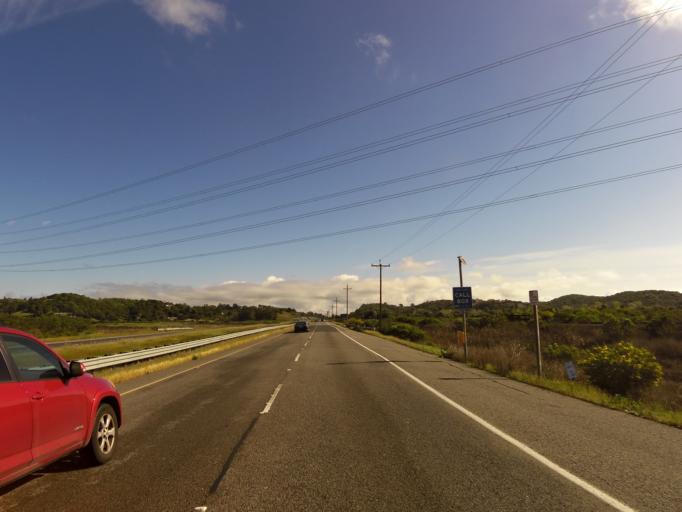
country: US
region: California
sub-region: Marin County
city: Black Point-Green Point
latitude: 38.0970
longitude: -122.5220
